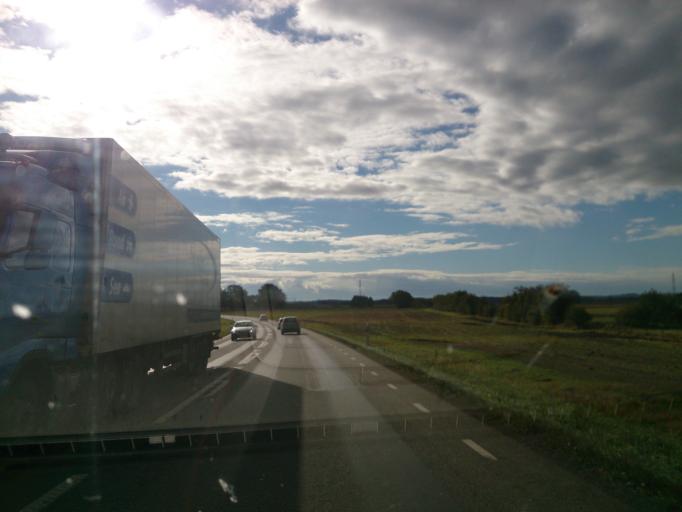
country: SE
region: Skane
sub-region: Sjobo Kommun
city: Sjoebo
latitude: 55.6306
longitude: 13.6816
